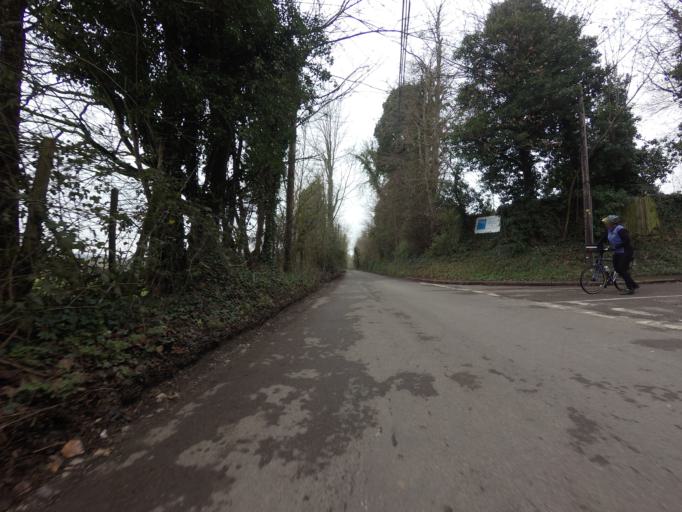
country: GB
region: England
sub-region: Kent
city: Eynsford
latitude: 51.3865
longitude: 0.2415
